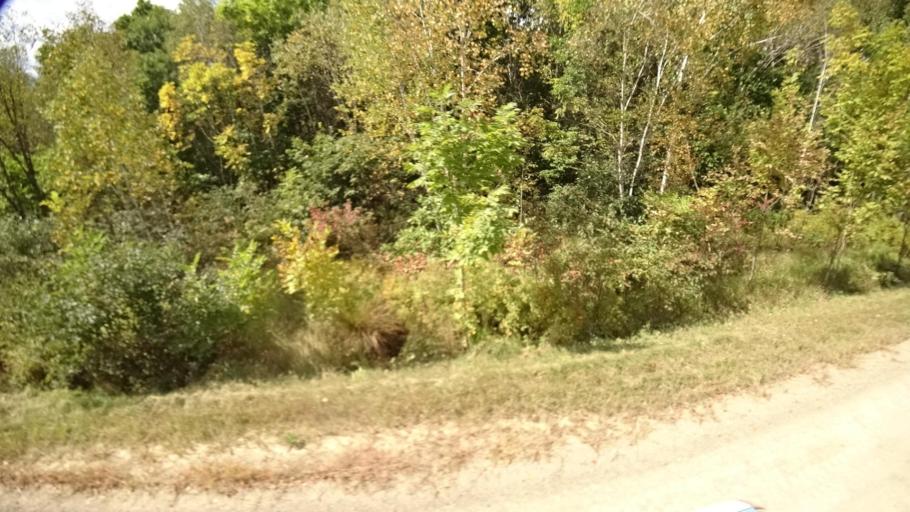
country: RU
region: Primorskiy
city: Yakovlevka
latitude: 44.7035
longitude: 133.6421
